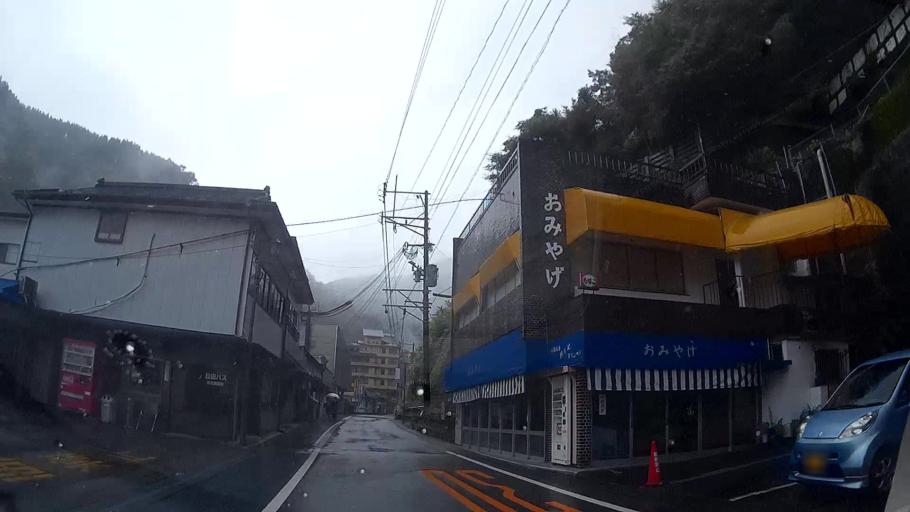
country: JP
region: Oita
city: Tsukawaki
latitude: 33.1835
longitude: 131.0343
